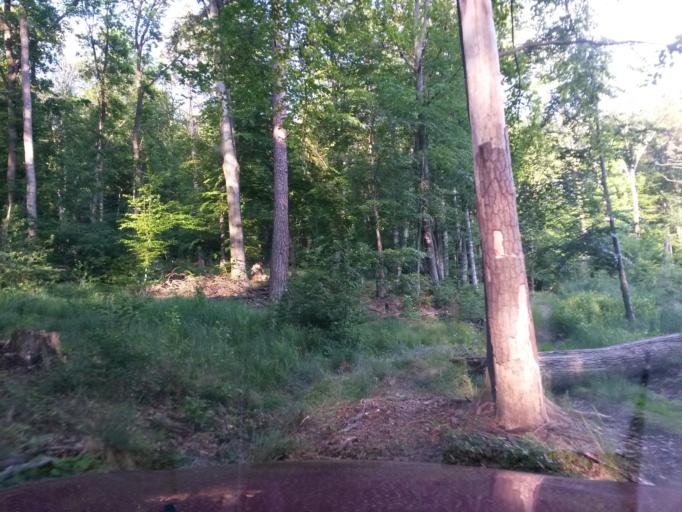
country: SK
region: Kosicky
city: Moldava nad Bodvou
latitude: 48.7327
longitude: 21.0445
